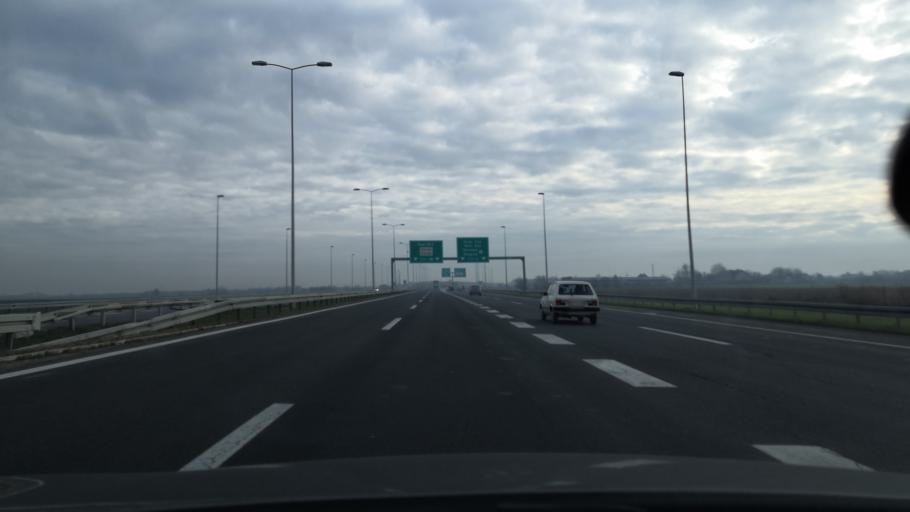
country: RS
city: Dobanovci
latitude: 44.8398
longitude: 20.2294
